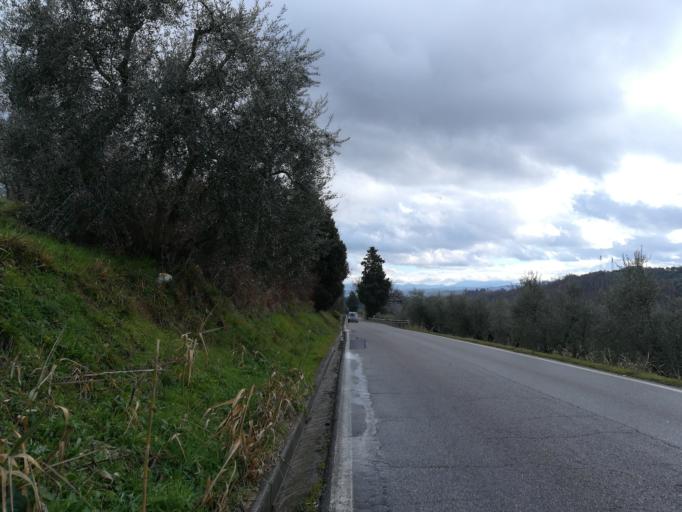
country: IT
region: Tuscany
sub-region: Provincia di Prato
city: Carmignano
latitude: 43.8045
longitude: 11.0335
